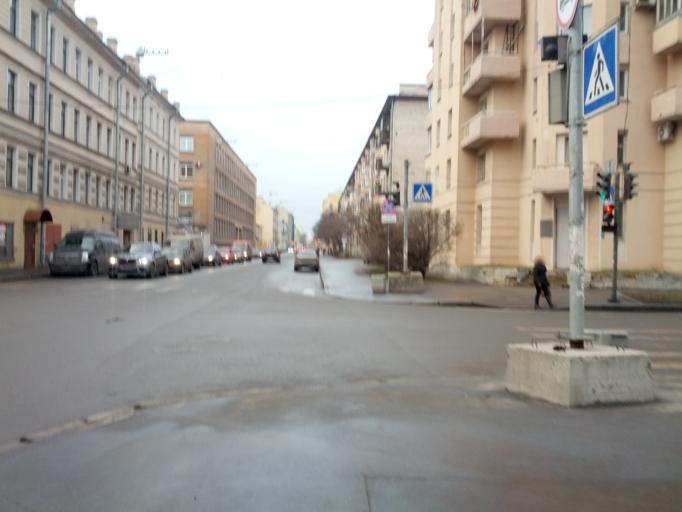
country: RU
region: St.-Petersburg
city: Centralniy
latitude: 59.9113
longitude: 30.3534
